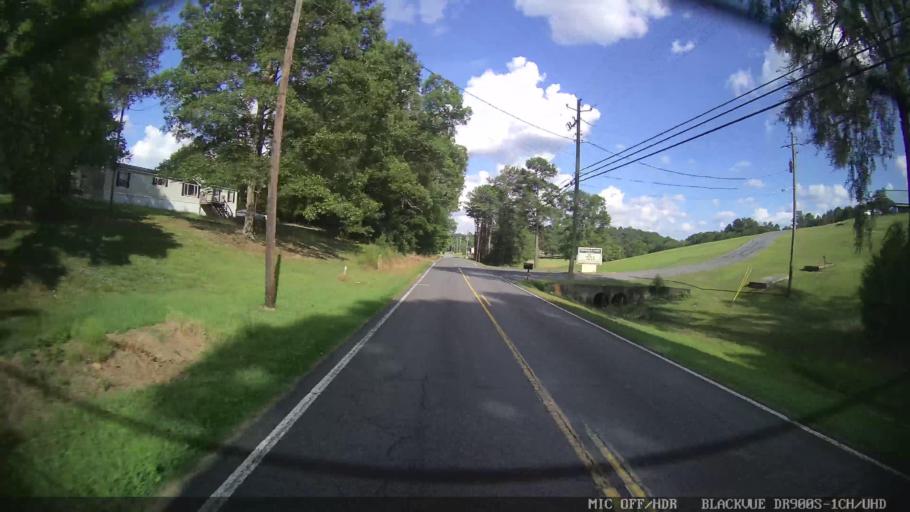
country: US
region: Georgia
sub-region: Floyd County
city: Lindale
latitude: 34.2014
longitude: -85.0907
